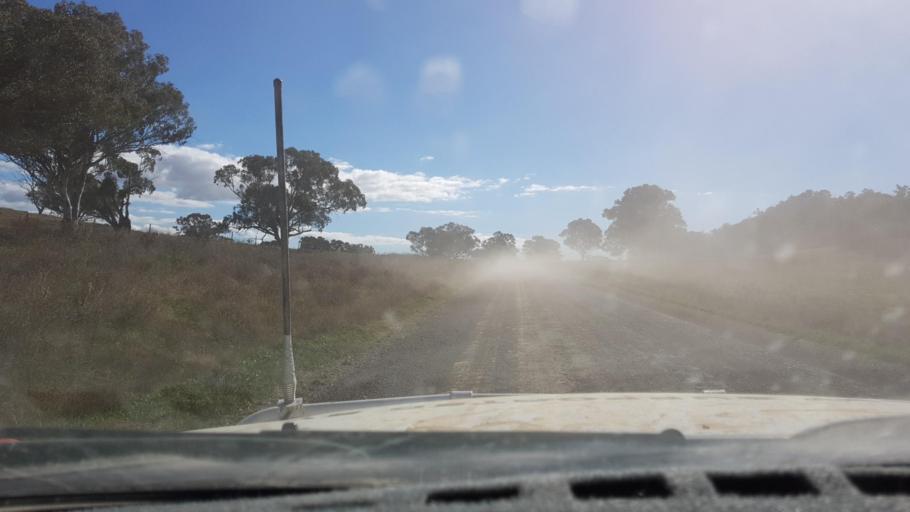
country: AU
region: New South Wales
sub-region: Narrabri
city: Blair Athol
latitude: -30.4373
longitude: 150.4570
